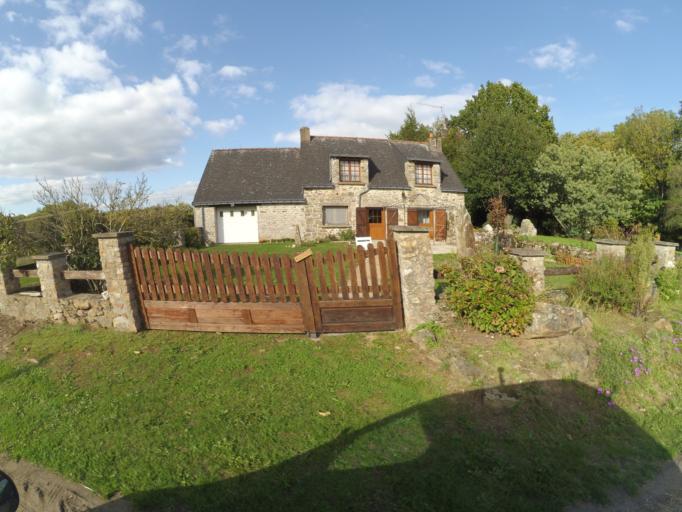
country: FR
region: Brittany
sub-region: Departement du Morbihan
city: Saint-Martin-sur-Oust
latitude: 47.7280
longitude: -2.2481
